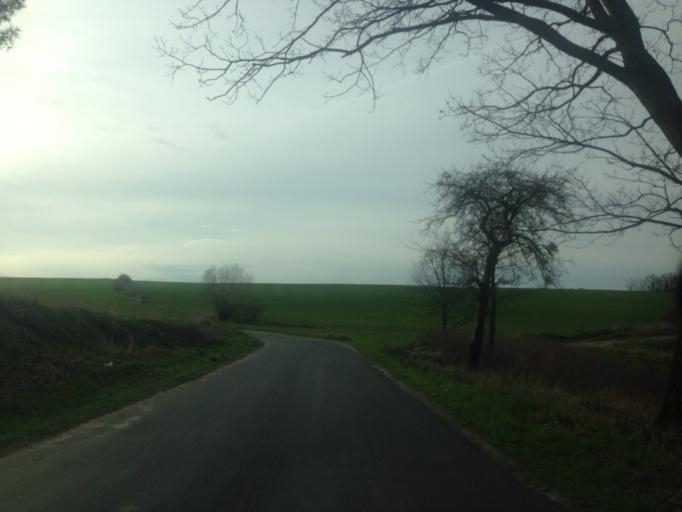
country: PL
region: Kujawsko-Pomorskie
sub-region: Powiat brodnicki
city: Jablonowo Pomorskie
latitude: 53.4510
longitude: 19.1801
